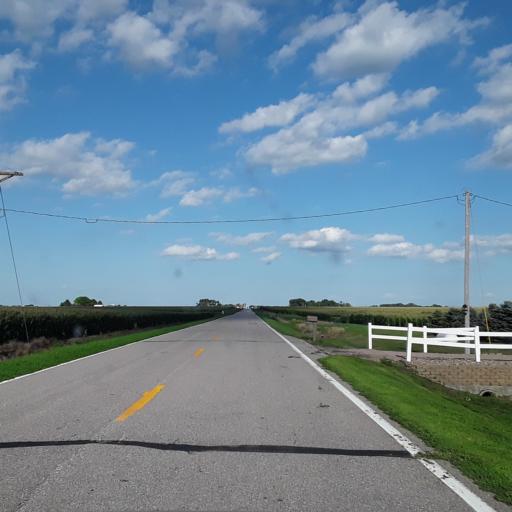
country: US
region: Nebraska
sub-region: Hall County
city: Wood River
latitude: 40.8878
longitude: -98.6211
